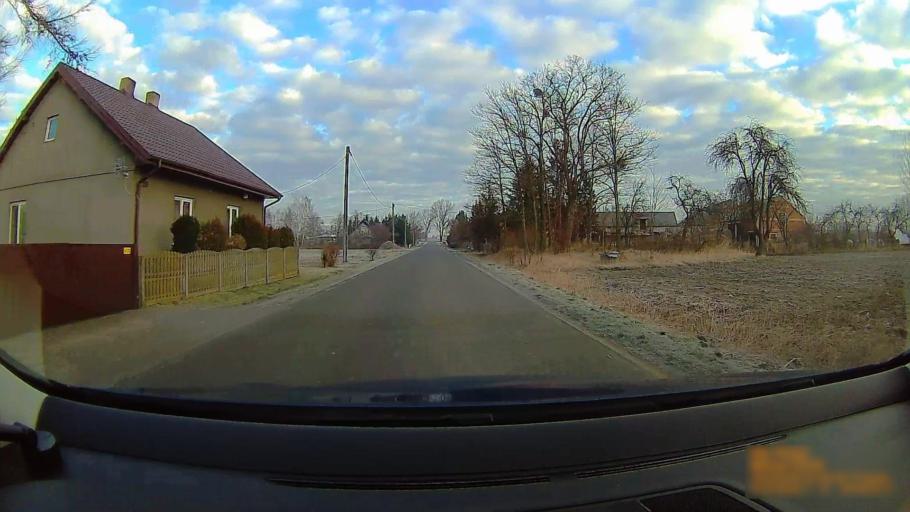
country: PL
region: Greater Poland Voivodeship
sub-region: Powiat koninski
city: Rzgow Pierwszy
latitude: 52.1437
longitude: 18.0558
